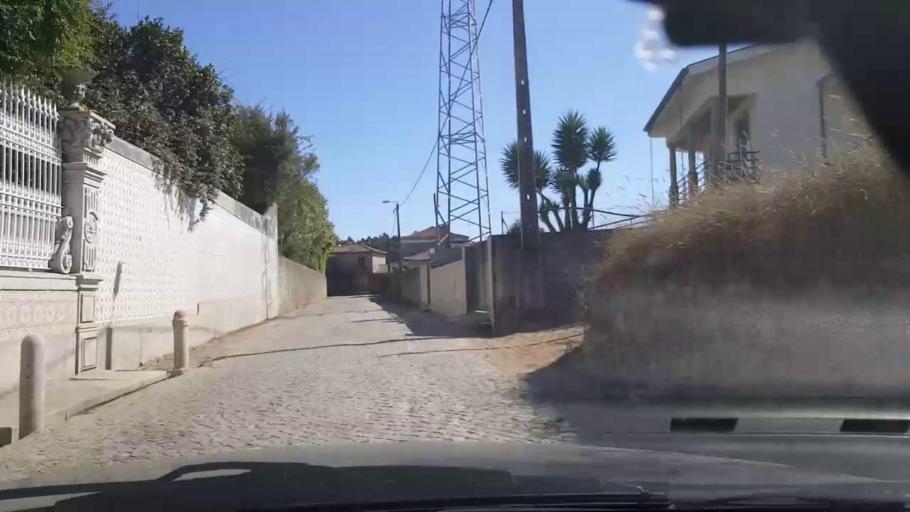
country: PT
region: Porto
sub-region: Vila do Conde
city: Arvore
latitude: 41.3185
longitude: -8.6976
